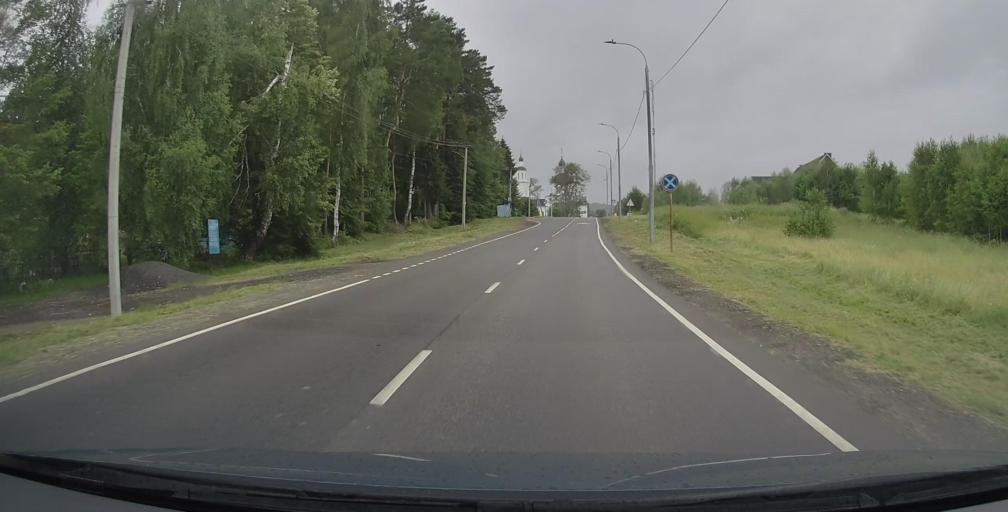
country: RU
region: Moskovskaya
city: Selyatino
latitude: 55.4269
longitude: 36.9631
